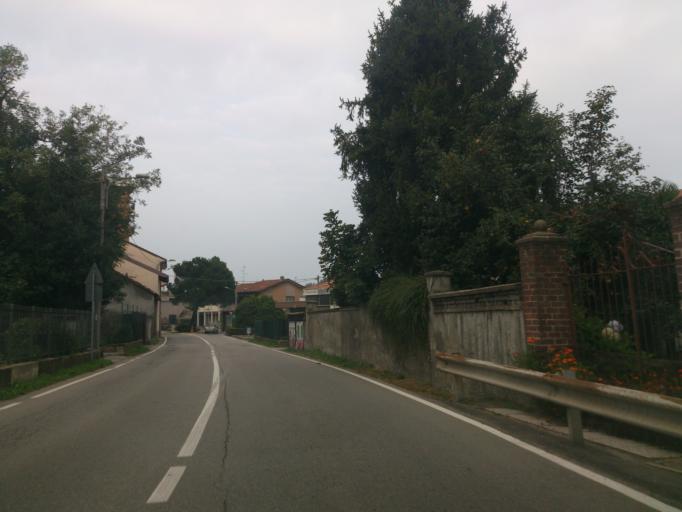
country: IT
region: Lombardy
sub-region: Provincia di Varese
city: Cassano Magnago
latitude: 45.6745
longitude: 8.8307
